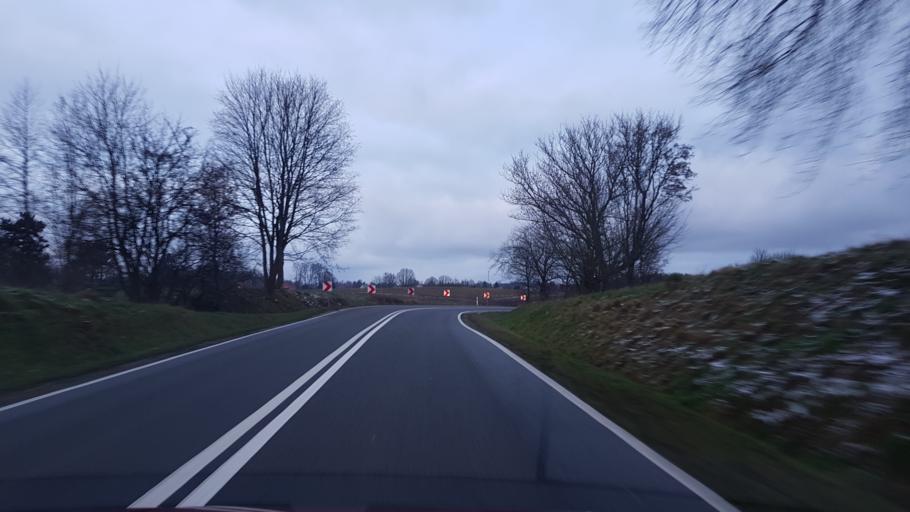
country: PL
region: Pomeranian Voivodeship
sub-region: Powiat bytowski
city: Tuchomie
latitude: 54.1012
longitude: 17.3213
